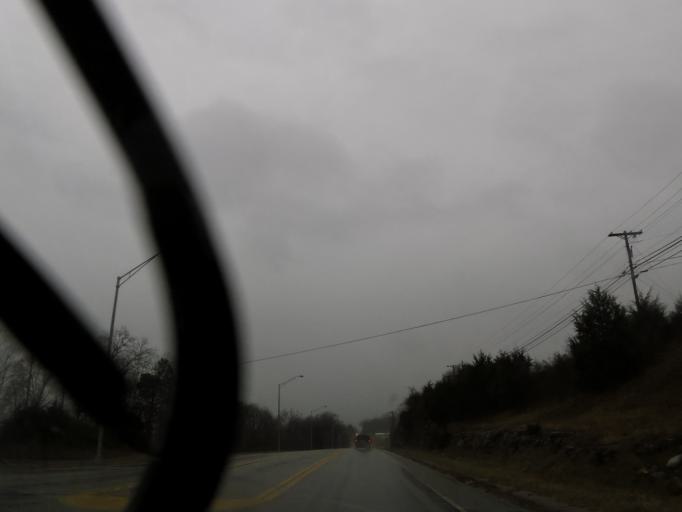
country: US
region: Kentucky
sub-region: Rockcastle County
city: Mount Vernon
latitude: 37.3501
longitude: -84.3662
